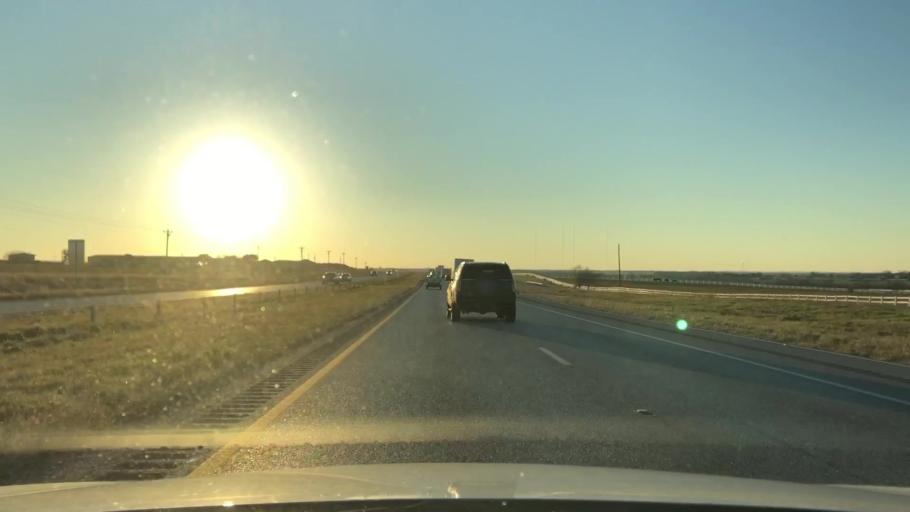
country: US
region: Texas
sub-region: Guadalupe County
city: Marion
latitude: 29.5329
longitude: -98.0999
